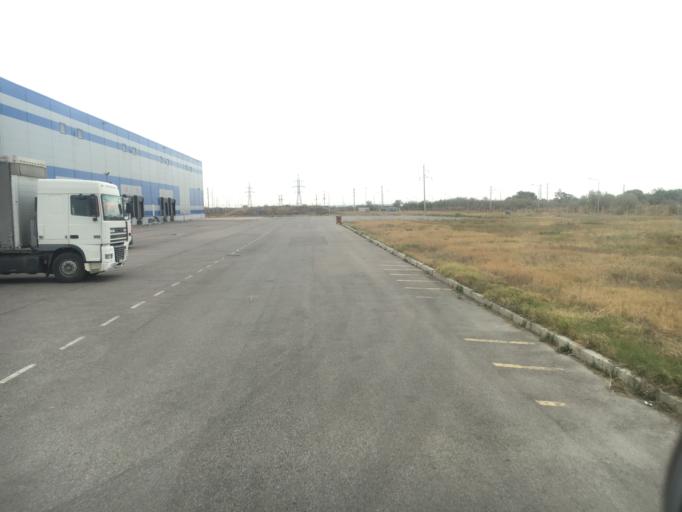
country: KZ
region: Almaty Oblysy
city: Energeticheskiy
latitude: 43.5850
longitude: 77.0954
